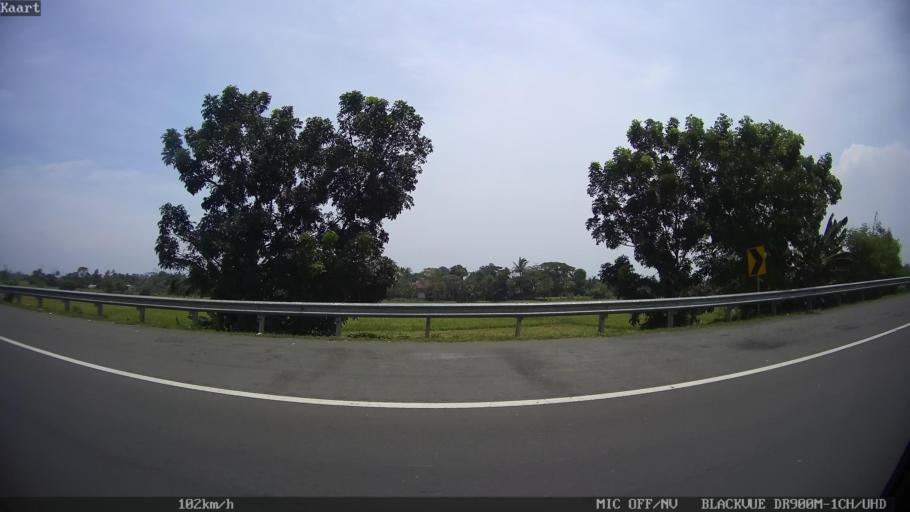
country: ID
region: West Java
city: Kresek
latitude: -6.1833
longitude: 106.3971
